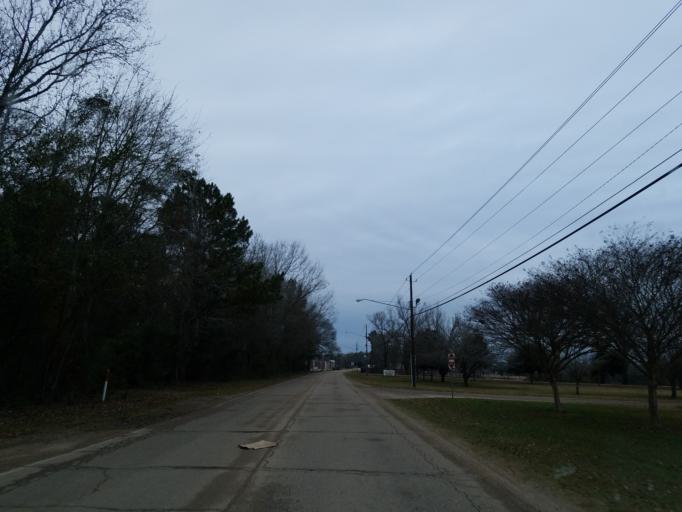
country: US
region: Mississippi
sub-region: Forrest County
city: Hattiesburg
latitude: 31.3089
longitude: -89.2799
